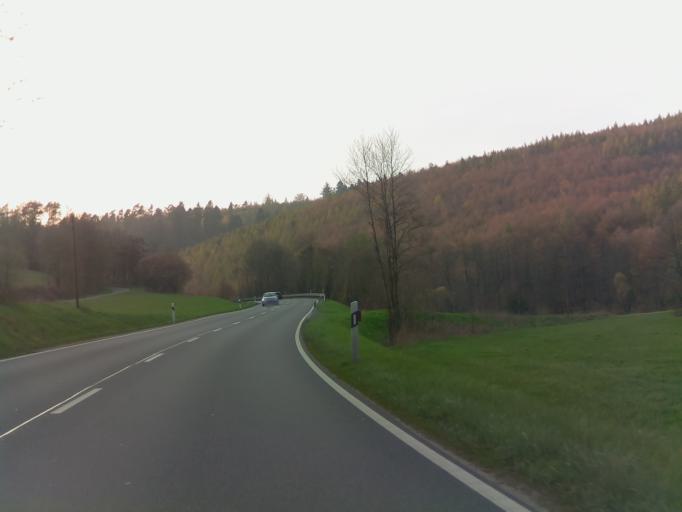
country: DE
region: Thuringia
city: Unterbreizbach
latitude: 50.8607
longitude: 9.9404
